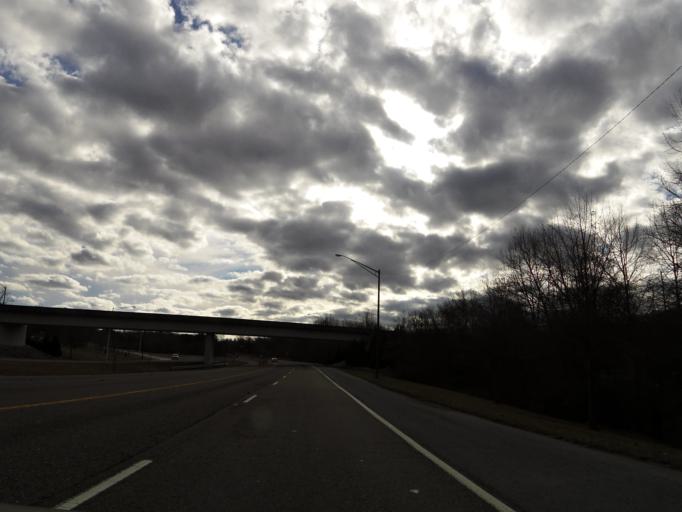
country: US
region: Tennessee
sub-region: Knox County
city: Knoxville
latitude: 35.9499
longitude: -83.8954
